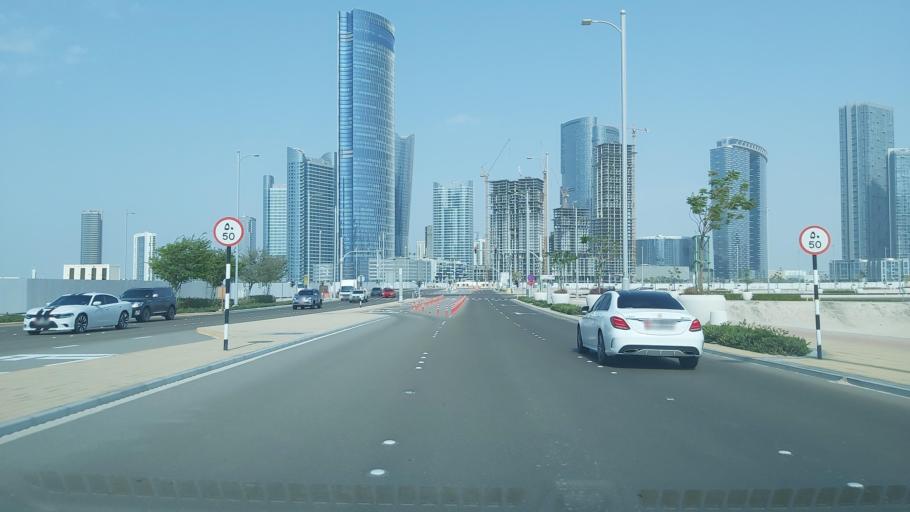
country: AE
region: Abu Dhabi
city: Abu Dhabi
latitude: 24.4977
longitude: 54.3963
